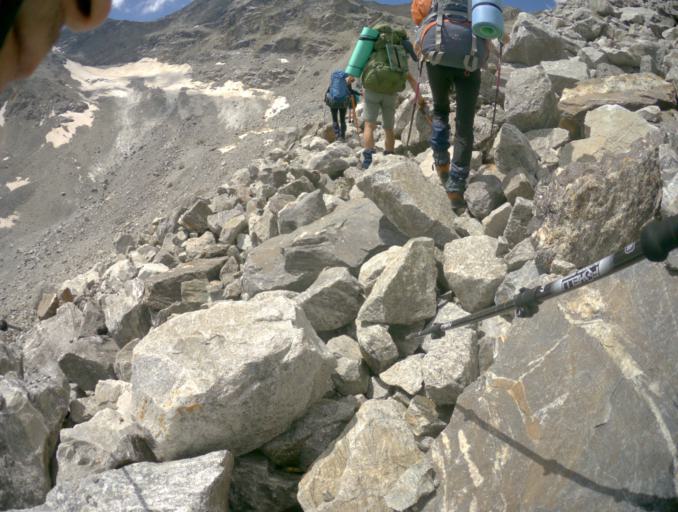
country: RU
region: Karachayevo-Cherkesiya
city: Uchkulan
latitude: 43.3224
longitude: 42.0873
